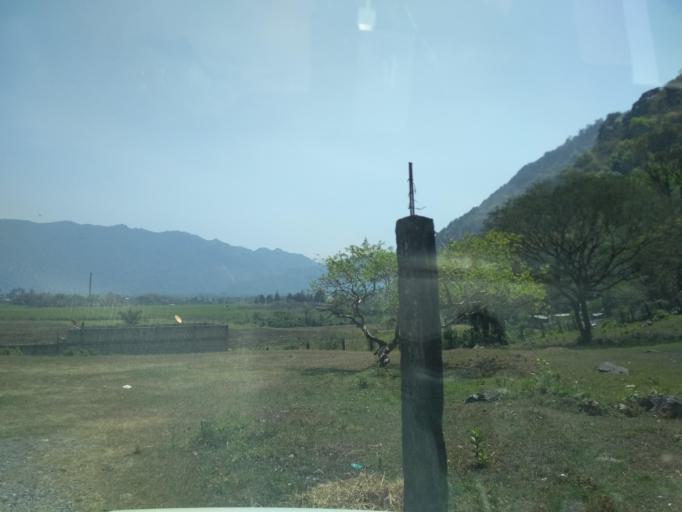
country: MX
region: Veracruz
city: Jalapilla
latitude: 18.8237
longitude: -97.1024
